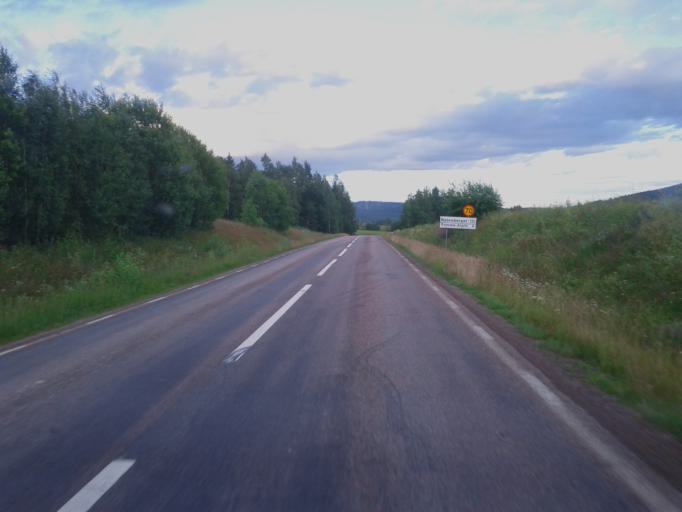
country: SE
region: Dalarna
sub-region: Borlange Kommun
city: Borlaenge
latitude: 60.4272
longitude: 15.3335
